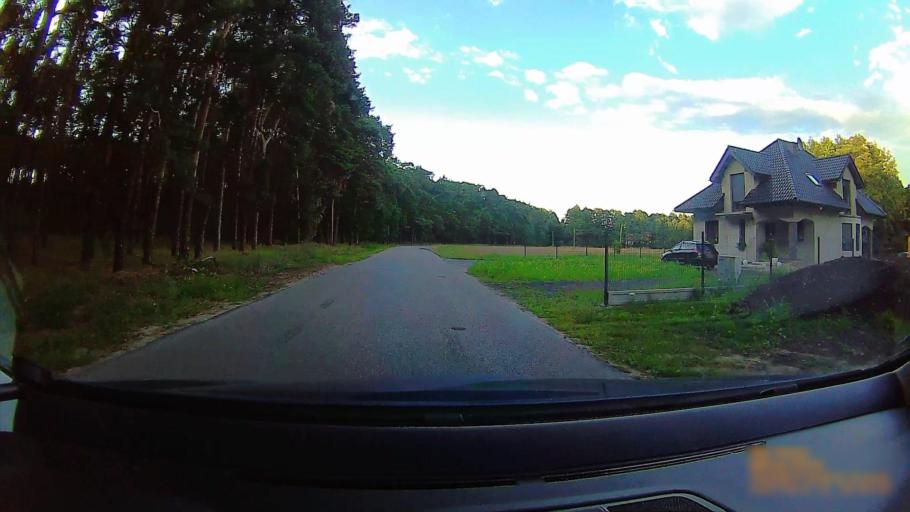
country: PL
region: Greater Poland Voivodeship
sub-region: Konin
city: Konin
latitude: 52.1991
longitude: 18.3170
